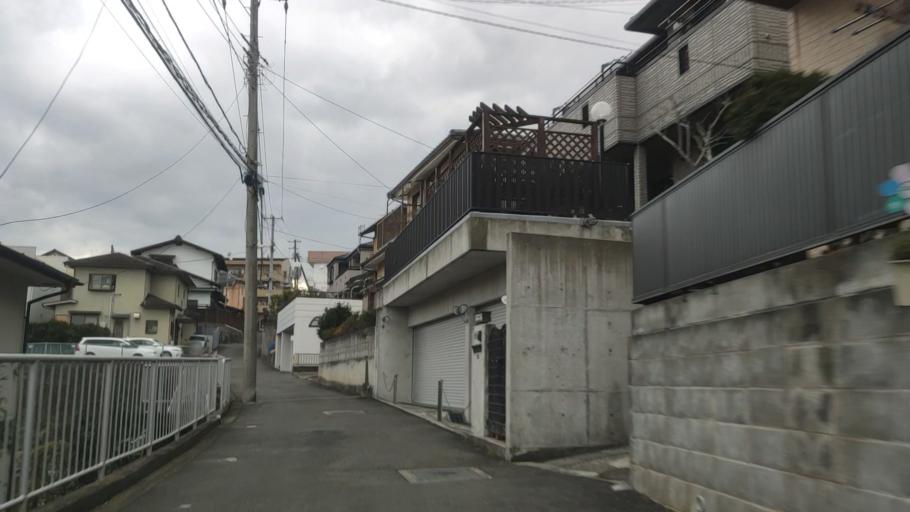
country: JP
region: Kanagawa
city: Odawara
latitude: 35.2595
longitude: 139.1533
